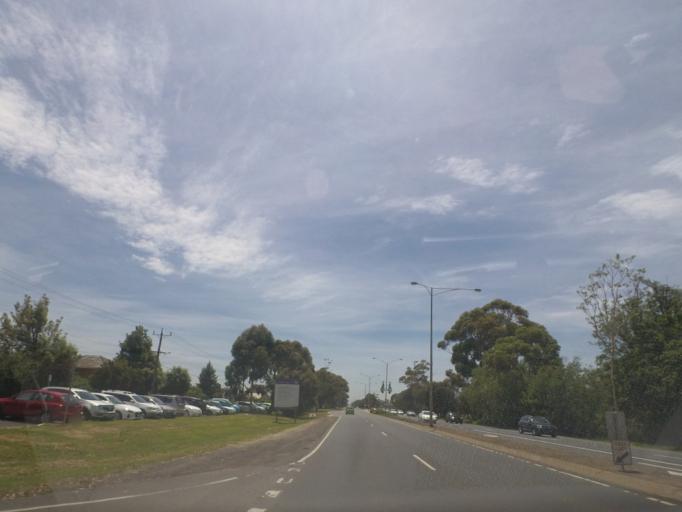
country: AU
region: Victoria
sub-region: Wyndham
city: Werribee
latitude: -37.8978
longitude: 144.6718
